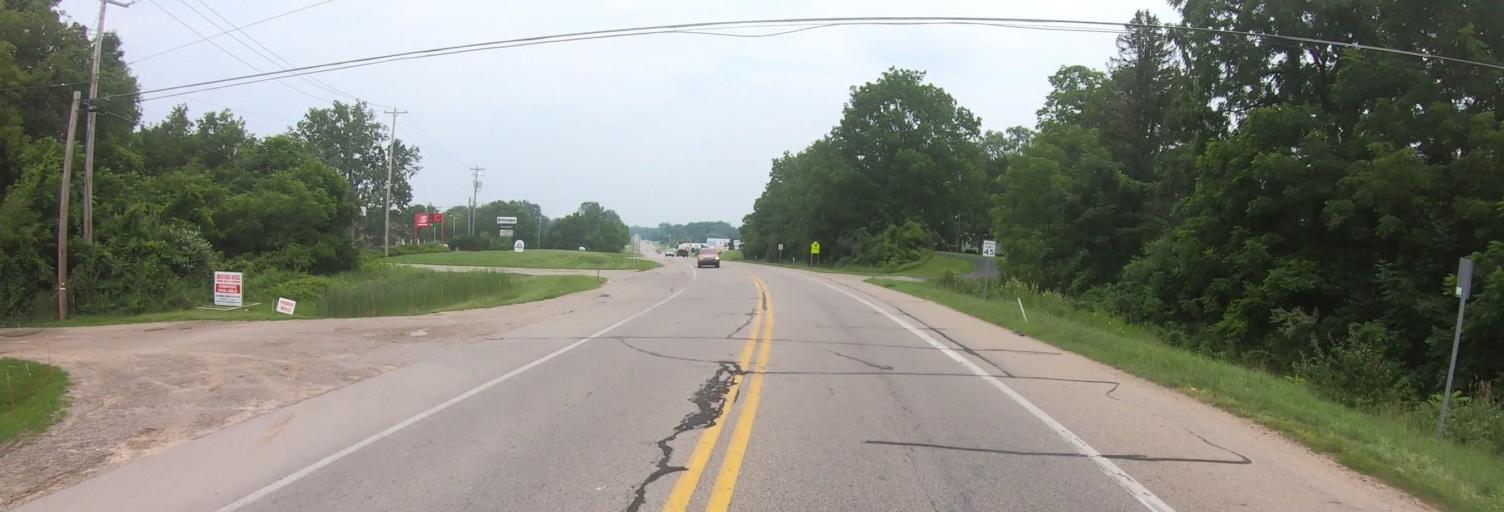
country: US
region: Michigan
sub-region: Ingham County
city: Haslett
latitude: 42.7752
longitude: -84.4081
